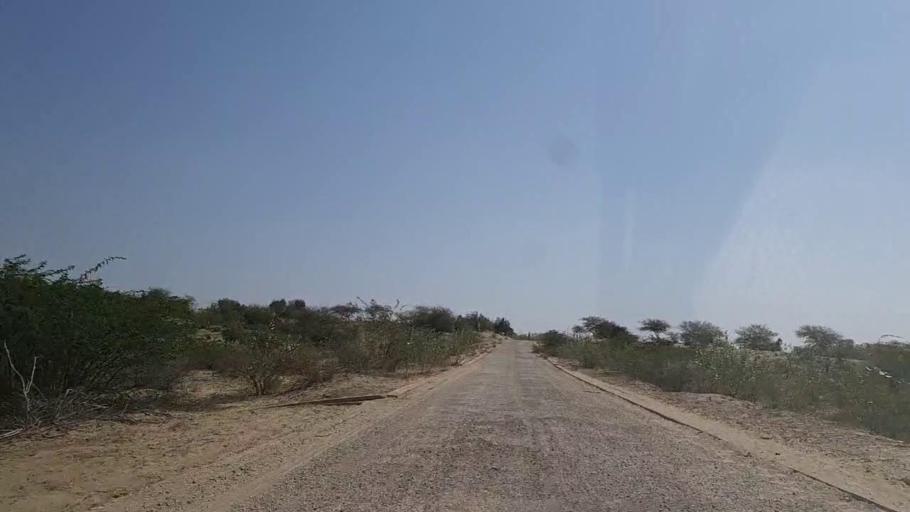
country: PK
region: Sindh
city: Diplo
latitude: 24.5133
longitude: 69.4190
